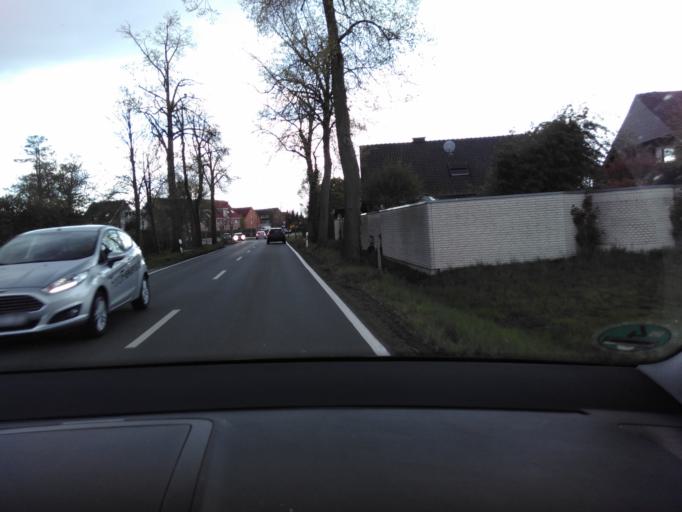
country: DE
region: North Rhine-Westphalia
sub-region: Regierungsbezirk Detmold
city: Guetersloh
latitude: 51.9299
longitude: 8.4454
